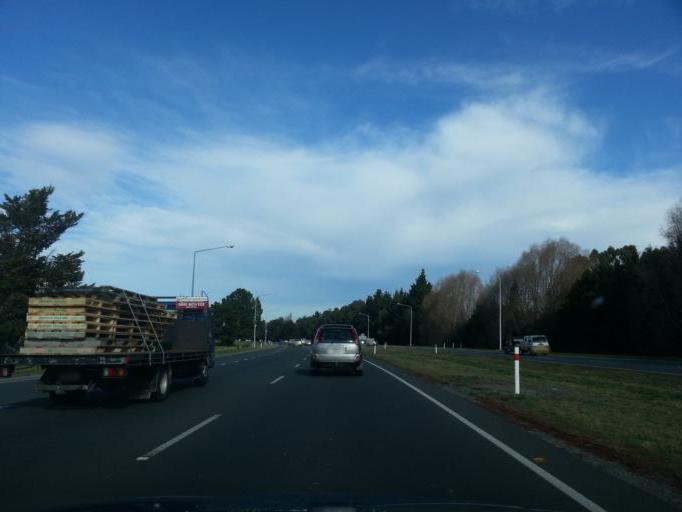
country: NZ
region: Canterbury
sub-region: Waimakariri District
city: Kaiapoi
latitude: -43.3895
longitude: 172.6400
